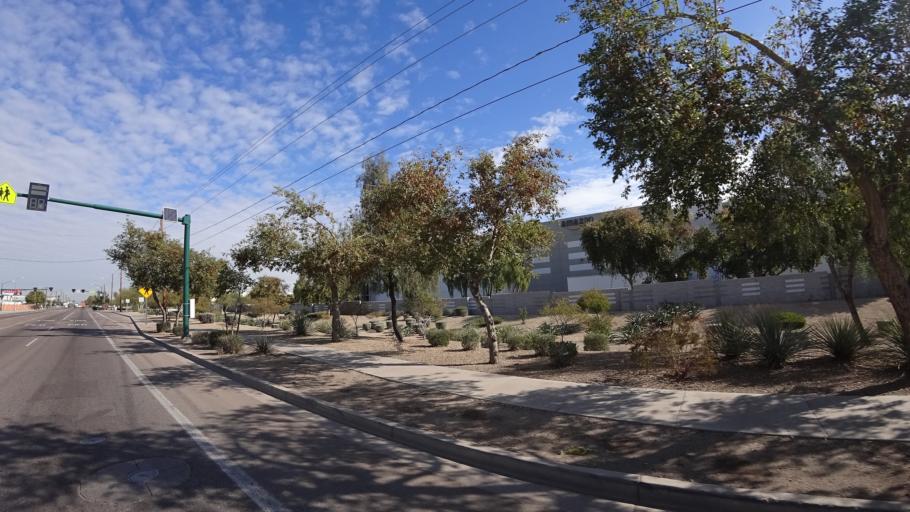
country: US
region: Arizona
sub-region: Maricopa County
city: Laveen
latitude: 33.4321
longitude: -112.1692
